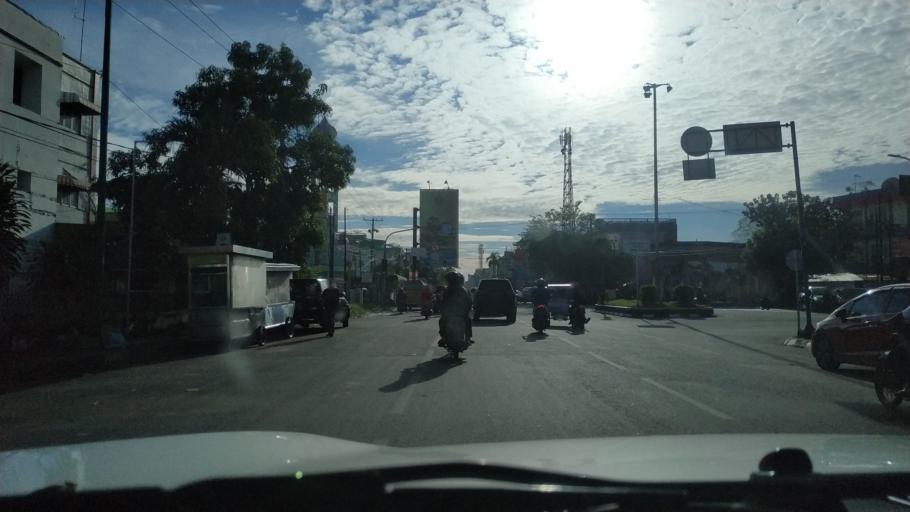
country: ID
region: North Sumatra
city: Medan
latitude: 3.5986
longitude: 98.6911
